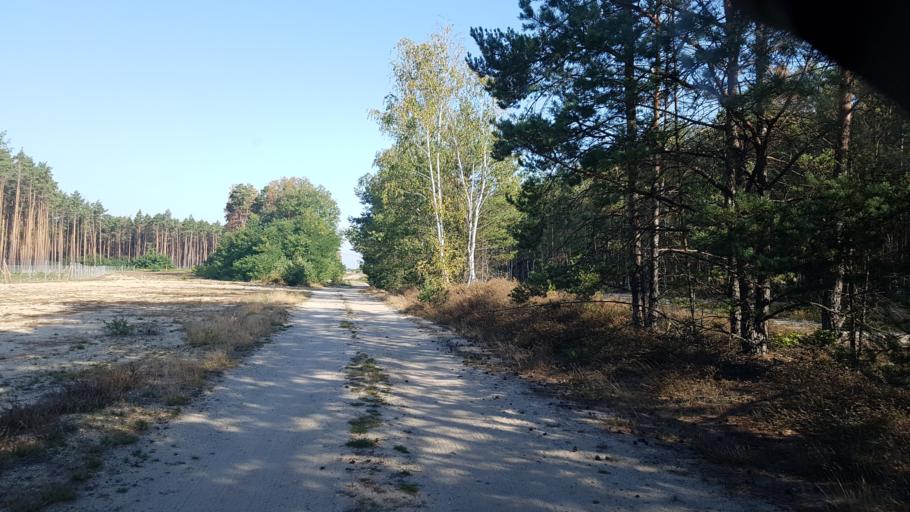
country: DE
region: Brandenburg
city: Finsterwalde
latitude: 51.6525
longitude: 13.6697
